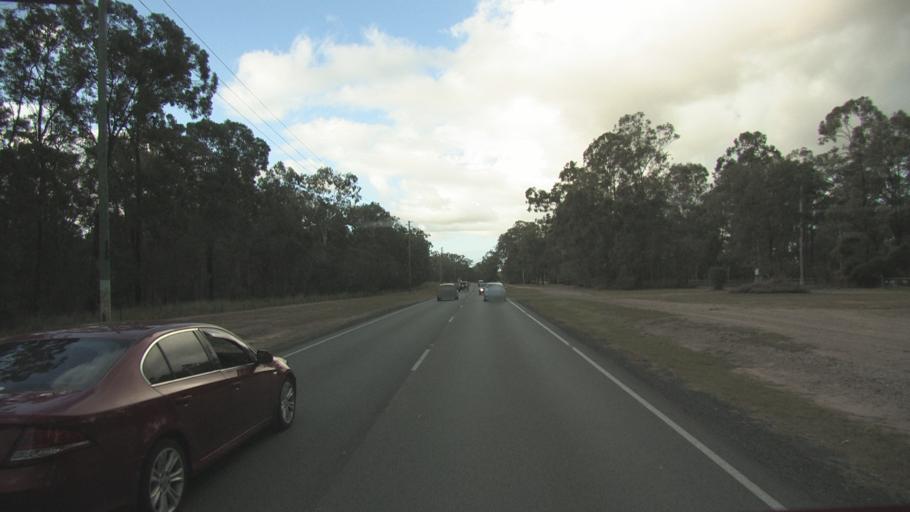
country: AU
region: Queensland
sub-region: Logan
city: Park Ridge South
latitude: -27.7117
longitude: 152.9965
